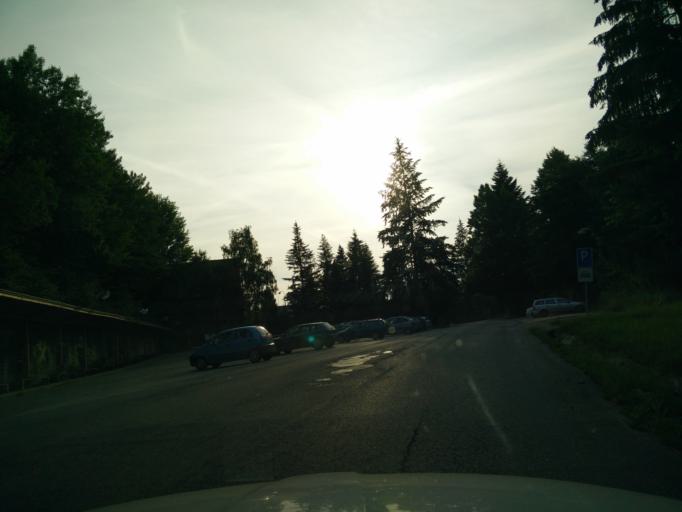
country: SK
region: Nitriansky
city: Prievidza
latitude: 48.7340
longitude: 18.6414
